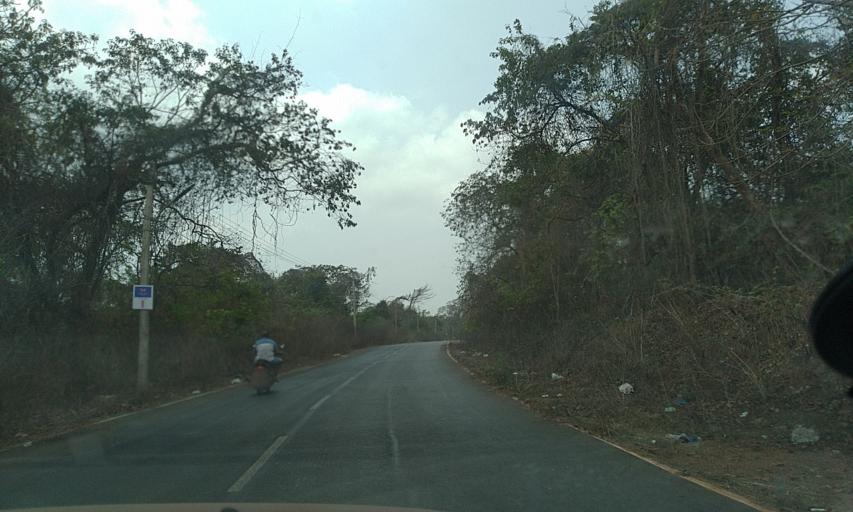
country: IN
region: Goa
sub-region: North Goa
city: Goa Velha
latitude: 15.4890
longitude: 73.9111
